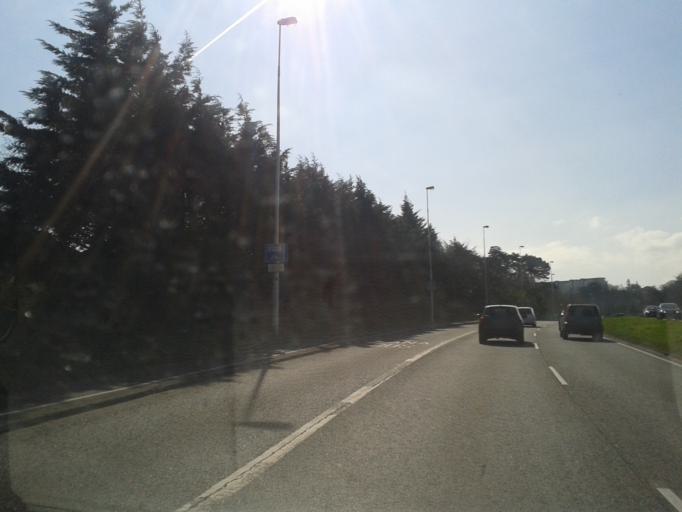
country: IE
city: Booterstown
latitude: 53.2877
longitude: -6.1944
